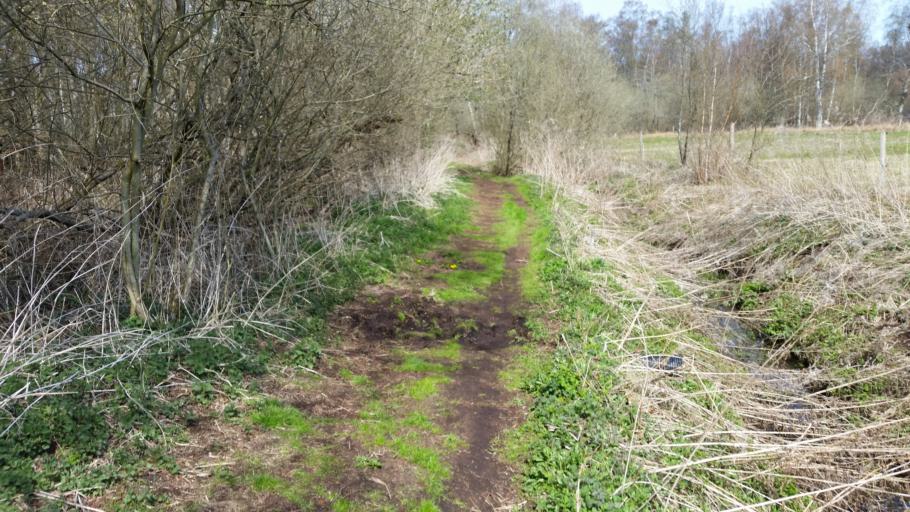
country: DK
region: Capital Region
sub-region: Helsingor Kommune
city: Hornbaek
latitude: 56.0766
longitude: 12.4096
